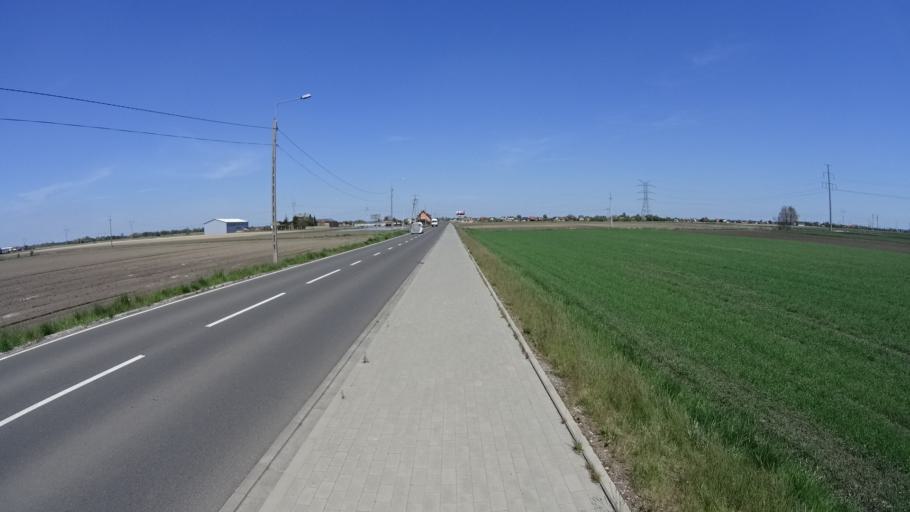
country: PL
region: Masovian Voivodeship
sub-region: Powiat warszawski zachodni
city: Jozefow
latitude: 52.2320
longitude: 20.7377
